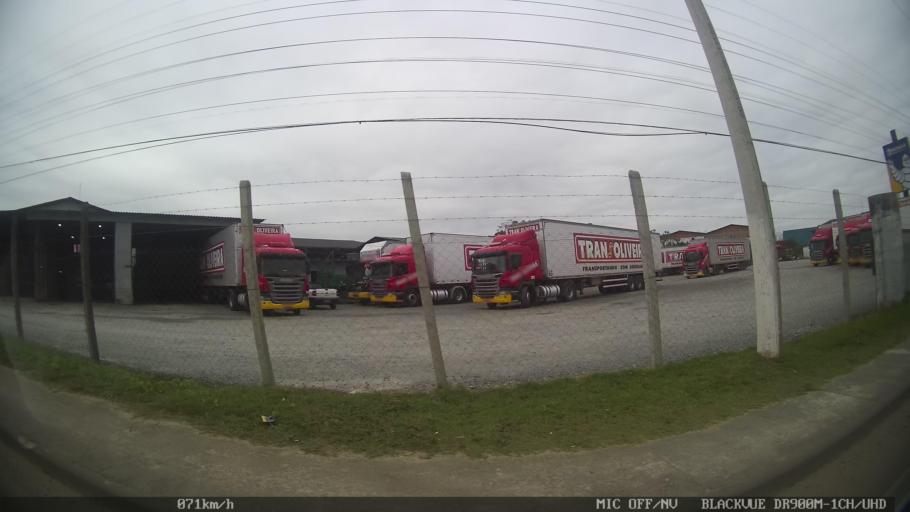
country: BR
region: Santa Catarina
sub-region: Joinville
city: Joinville
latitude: -26.2837
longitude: -48.8884
